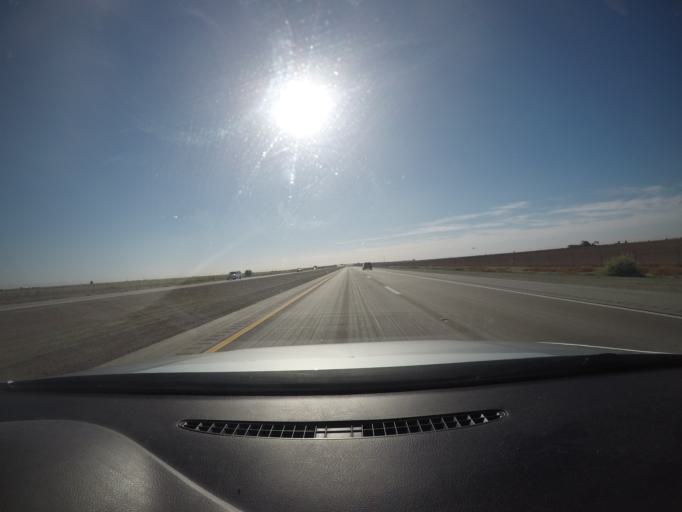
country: US
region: California
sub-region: Imperial County
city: Holtville
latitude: 32.7732
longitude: -115.3144
